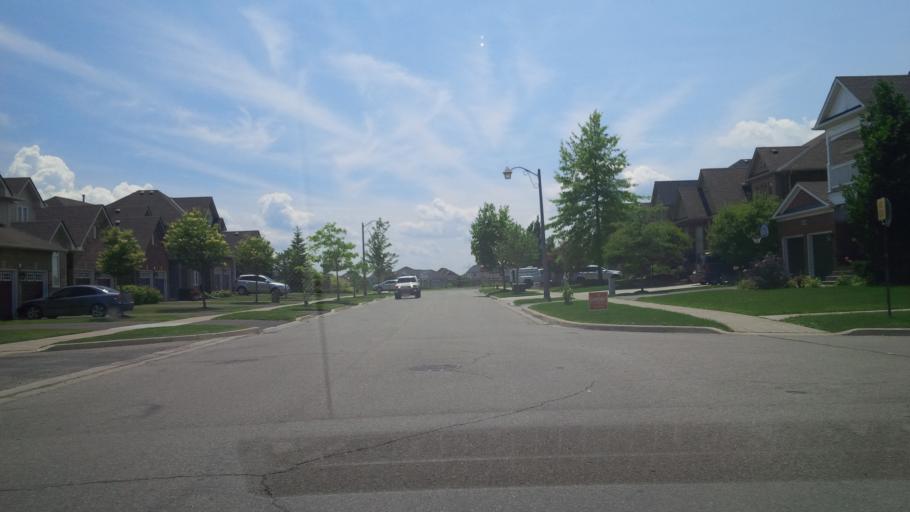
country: CA
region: Ontario
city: Burlington
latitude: 43.4000
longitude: -79.8085
